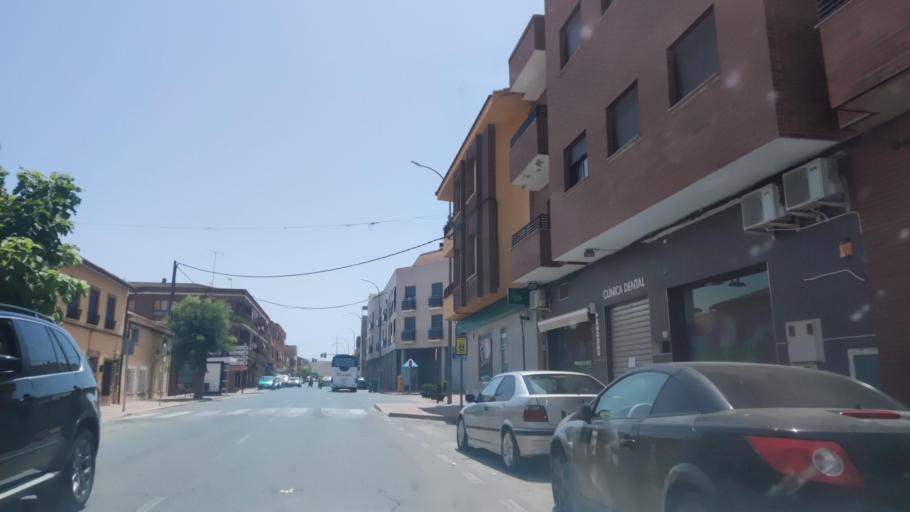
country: ES
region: Castille-La Mancha
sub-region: Provincia de Albacete
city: Pozo-Canada
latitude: 38.8043
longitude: -1.7330
